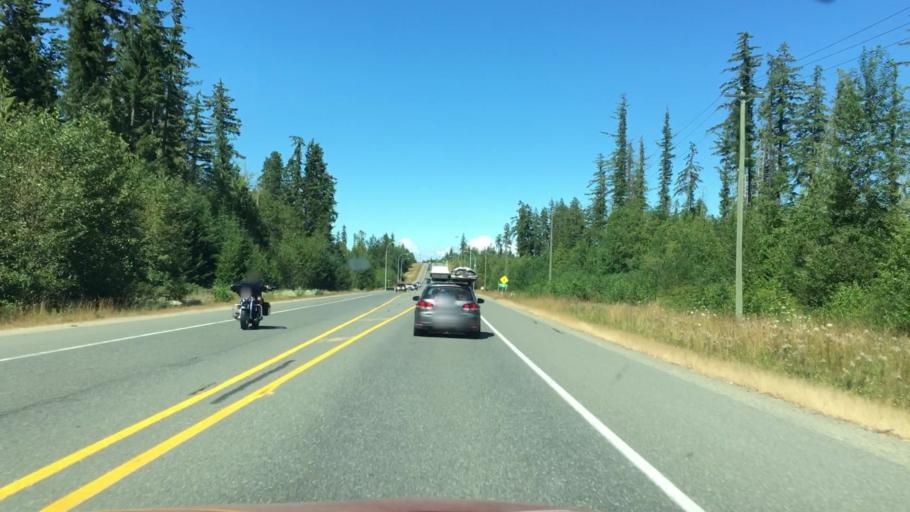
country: CA
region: British Columbia
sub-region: Regional District of Nanaimo
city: Parksville
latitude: 49.3134
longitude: -124.4482
